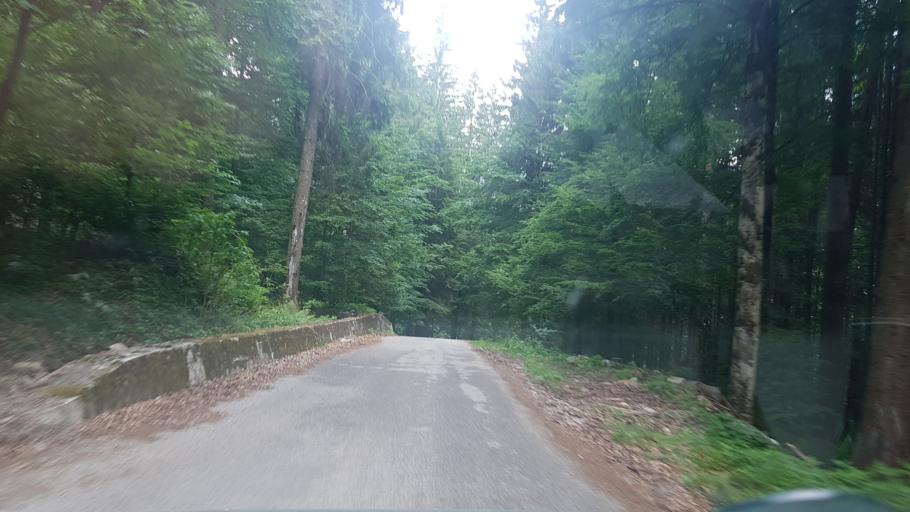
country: IT
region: Friuli Venezia Giulia
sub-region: Provincia di Udine
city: Paularo
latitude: 46.5356
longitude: 13.2080
